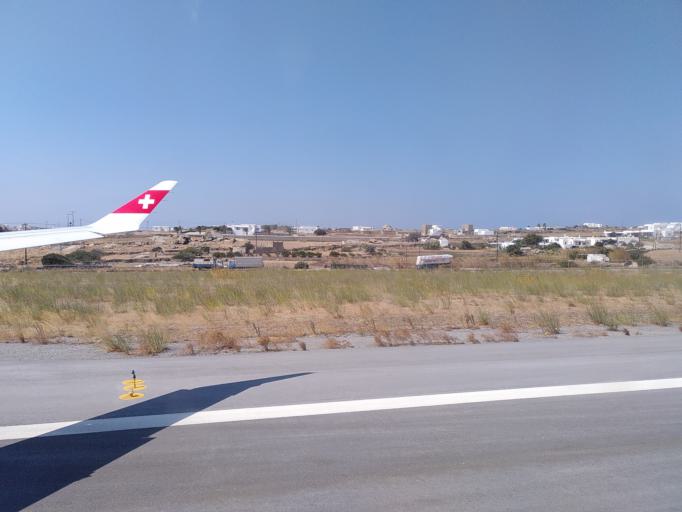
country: GR
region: South Aegean
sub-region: Nomos Kykladon
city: Mykonos
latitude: 37.4280
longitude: 25.3514
